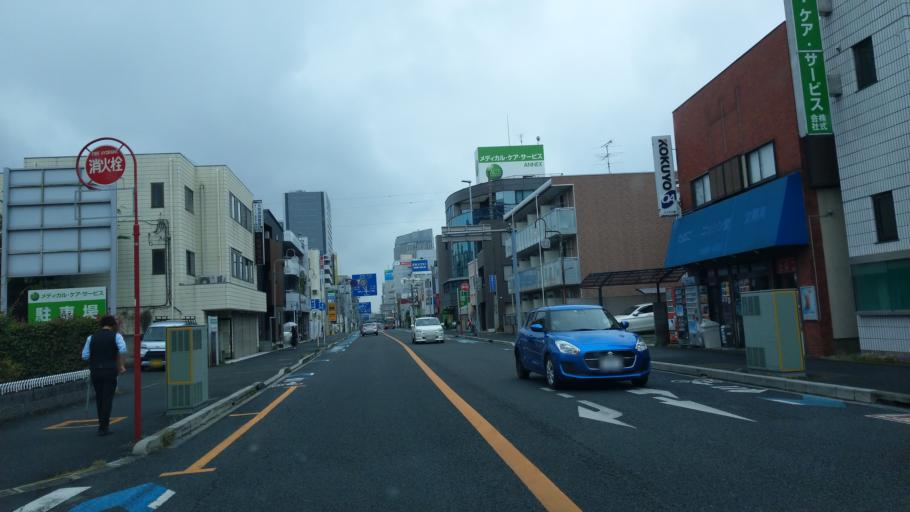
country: JP
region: Saitama
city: Yono
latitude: 35.9098
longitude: 139.6158
